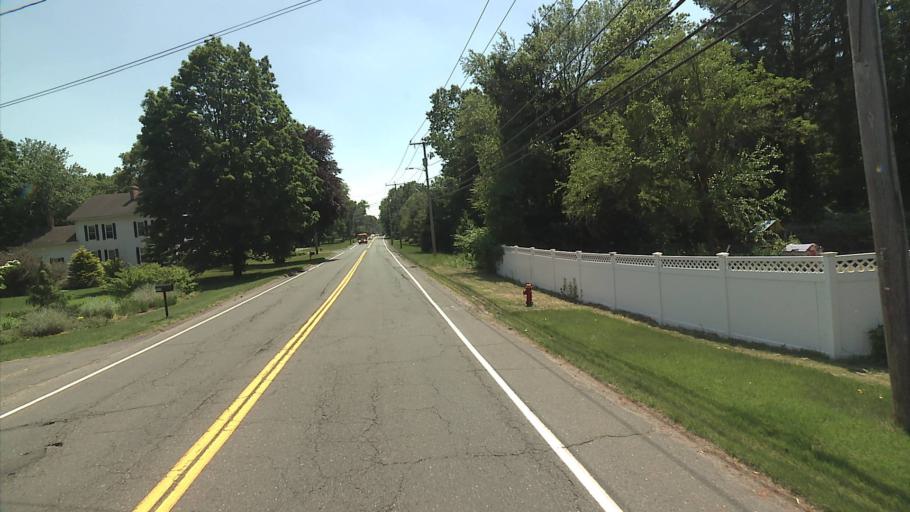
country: US
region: Connecticut
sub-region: Hartford County
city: South Windsor
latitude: 41.8196
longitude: -72.5889
